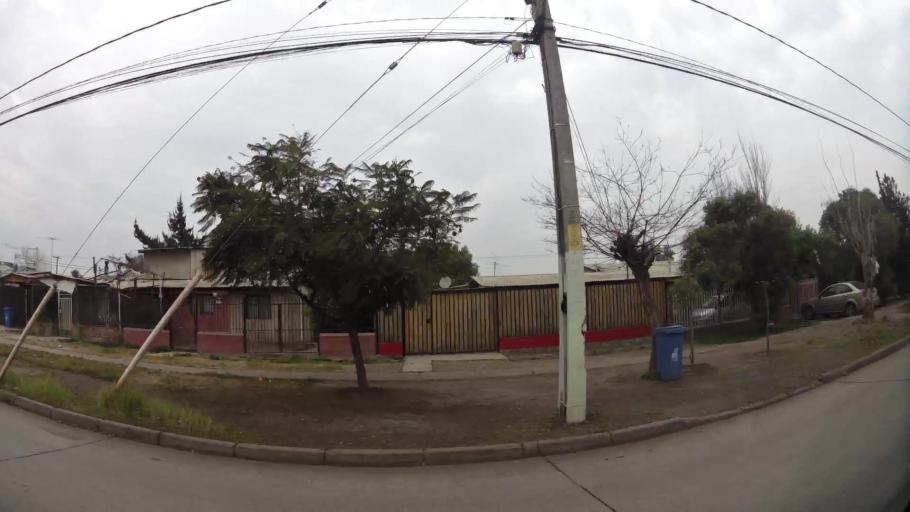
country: CL
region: Santiago Metropolitan
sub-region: Provincia de Chacabuco
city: Chicureo Abajo
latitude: -33.2098
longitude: -70.6828
